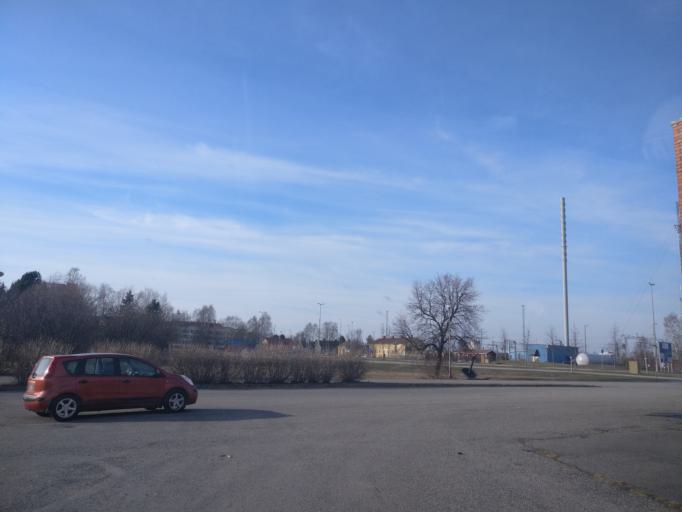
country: FI
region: Lapland
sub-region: Kemi-Tornio
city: Kemi
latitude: 65.7308
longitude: 24.5776
